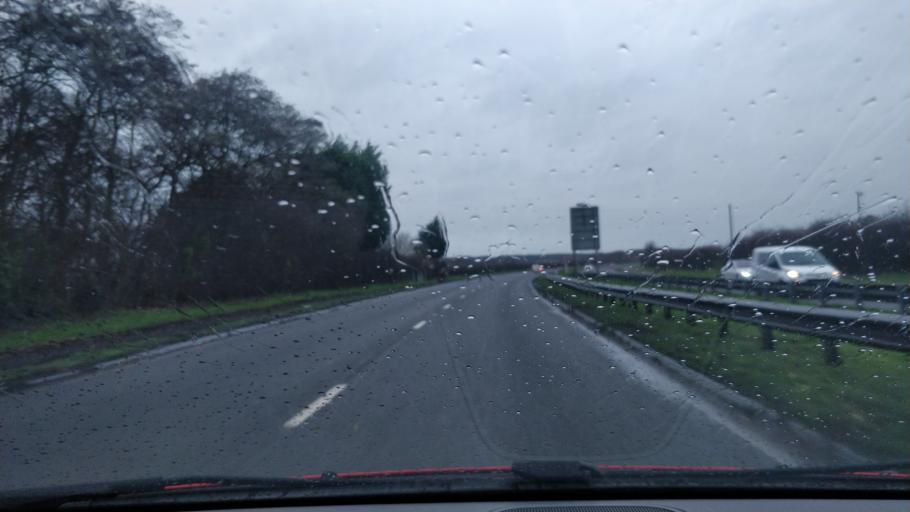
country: GB
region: England
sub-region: Sefton
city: Formby
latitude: 53.5713
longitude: -3.0498
